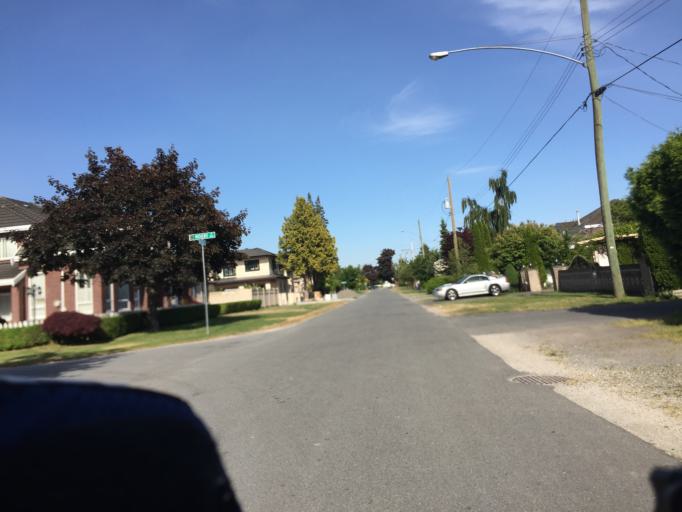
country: CA
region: British Columbia
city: Richmond
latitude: 49.1494
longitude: -123.1340
